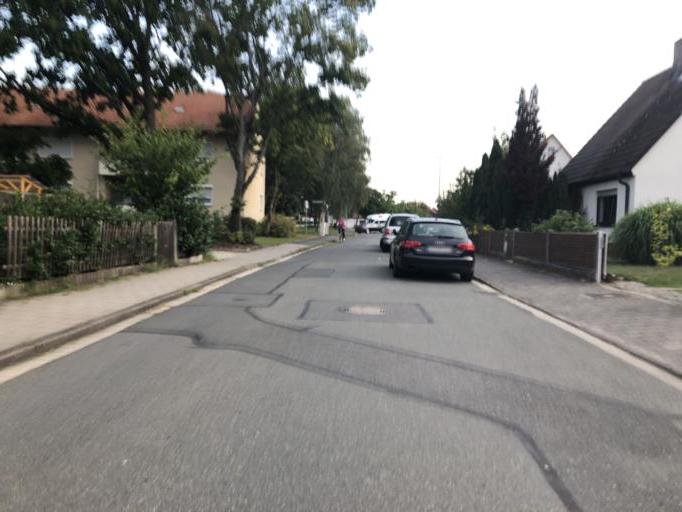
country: DE
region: Bavaria
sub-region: Regierungsbezirk Mittelfranken
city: Erlangen
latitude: 49.5923
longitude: 10.9780
